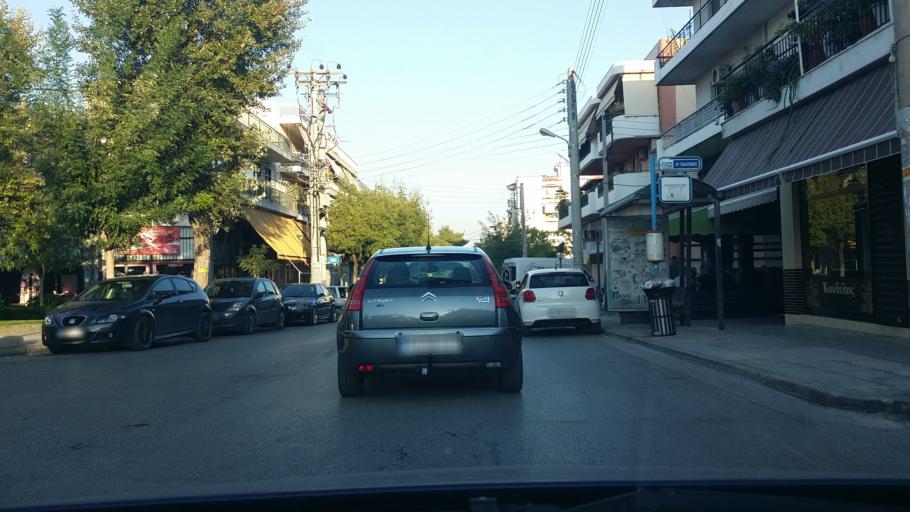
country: GR
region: Attica
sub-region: Nomarchia Athinas
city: Ilion
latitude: 38.0293
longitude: 23.6925
